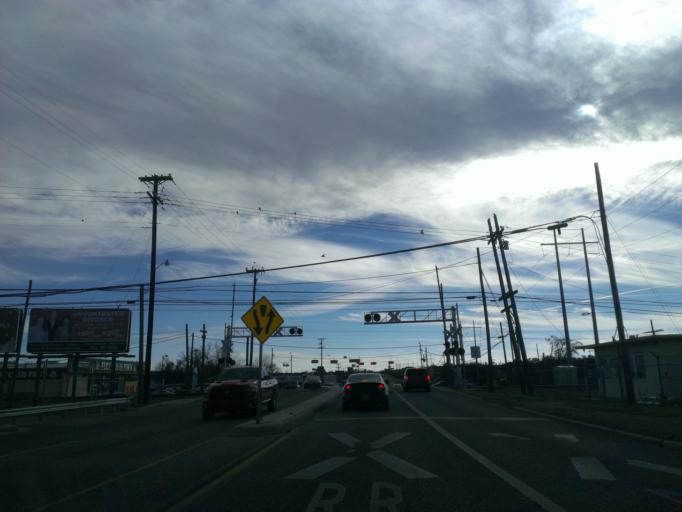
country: US
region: Texas
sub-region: Bell County
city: Killeen
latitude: 31.1219
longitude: -97.7425
